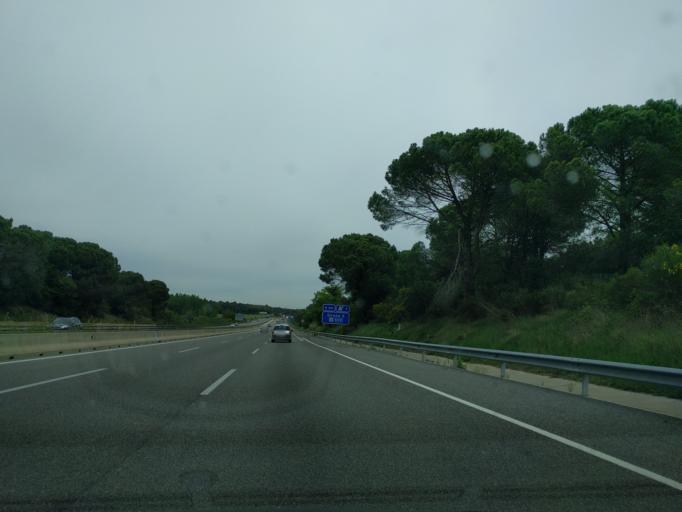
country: ES
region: Catalonia
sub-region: Provincia de Girona
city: Aiguaviva
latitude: 41.9113
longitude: 2.7735
